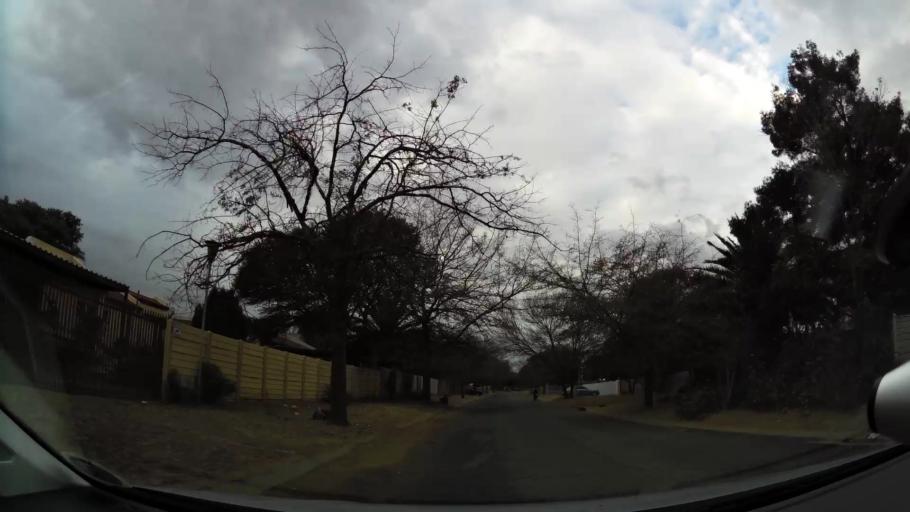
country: ZA
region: Orange Free State
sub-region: Lejweleputswa District Municipality
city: Welkom
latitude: -27.9512
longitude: 26.7307
